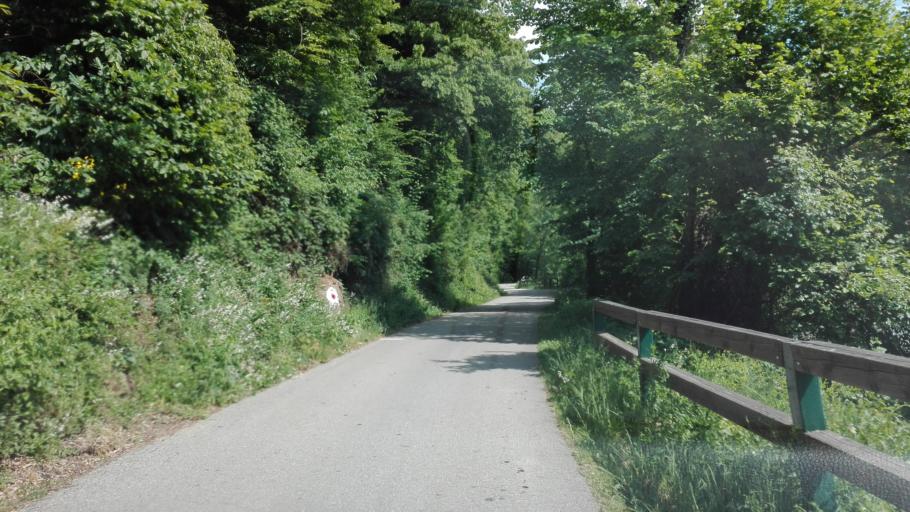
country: AT
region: Upper Austria
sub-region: Politischer Bezirk Rohrbach
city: Pfarrkirchen im Muehlkreis
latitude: 48.4364
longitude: 13.8677
